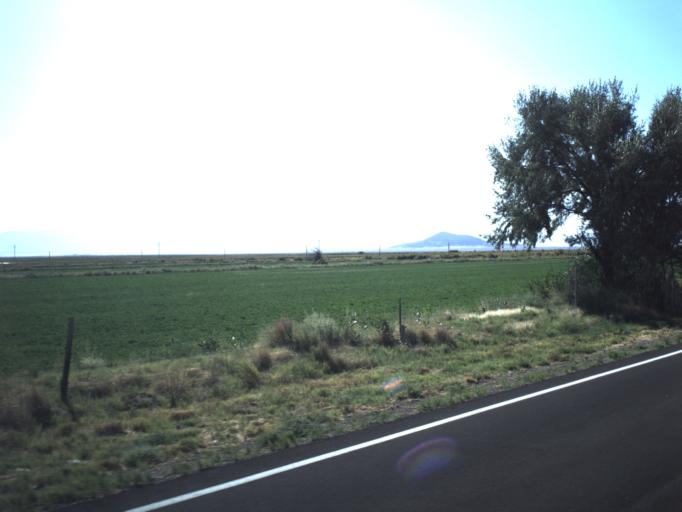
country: US
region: Utah
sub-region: Millard County
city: Delta
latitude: 39.2637
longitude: -112.6532
